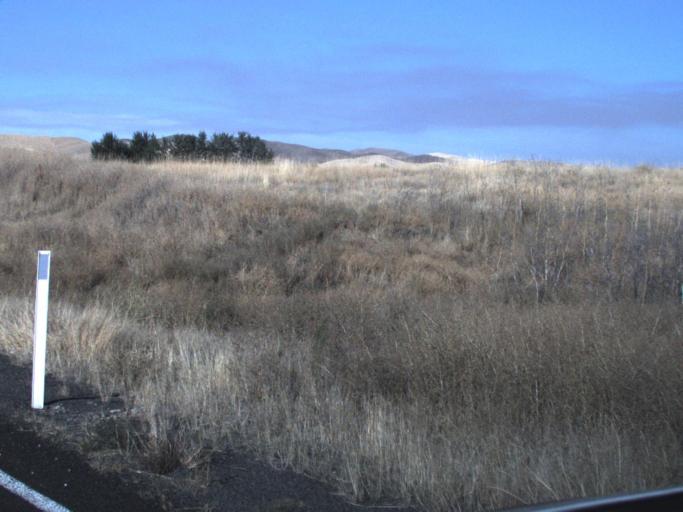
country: US
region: Washington
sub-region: Walla Walla County
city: Waitsburg
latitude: 46.2927
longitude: -118.3397
